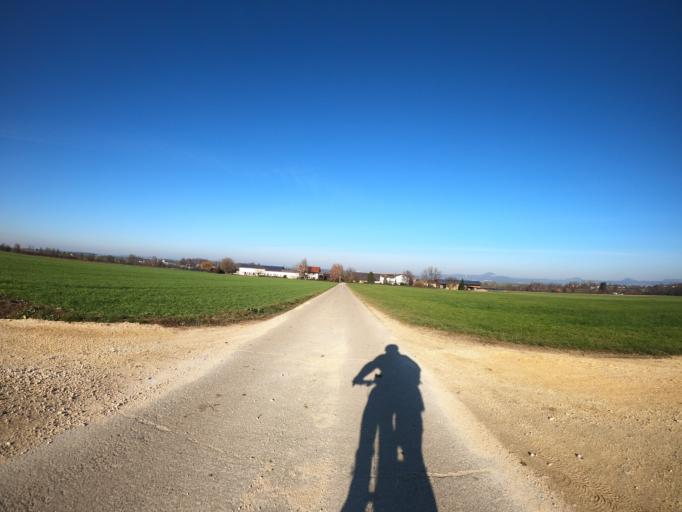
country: DE
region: Baden-Wuerttemberg
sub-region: Regierungsbezirk Stuttgart
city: Gammelshausen
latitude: 48.6467
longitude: 9.6524
